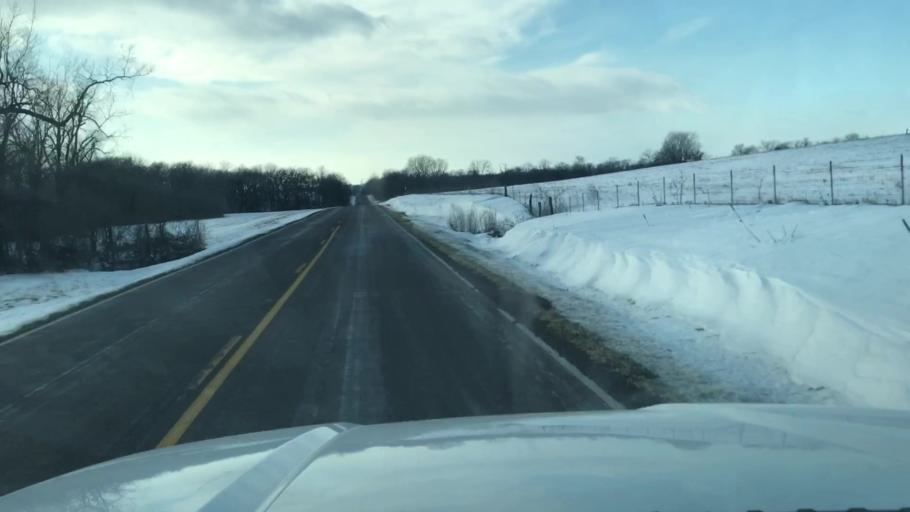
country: US
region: Missouri
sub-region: Nodaway County
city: Maryville
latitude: 40.2019
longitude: -94.9387
